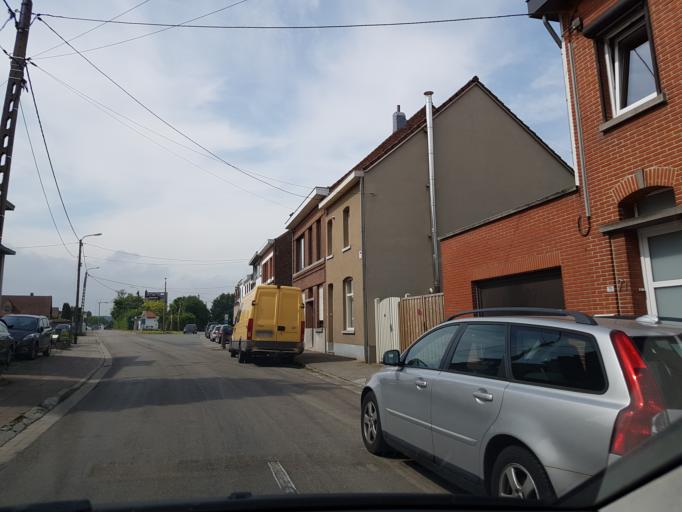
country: BE
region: Flanders
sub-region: Provincie Vlaams-Brabant
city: Meise
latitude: 50.9495
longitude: 4.3075
